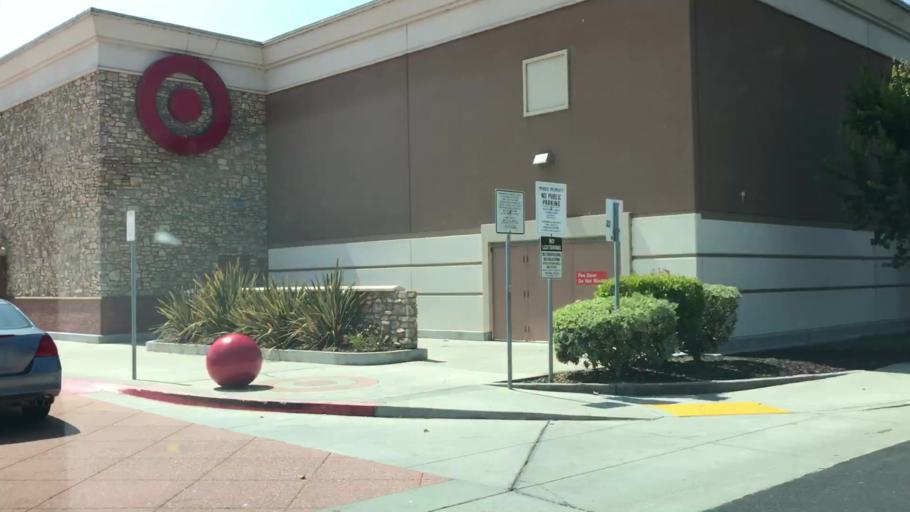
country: US
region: California
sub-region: Alameda County
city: San Lorenzo
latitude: 37.6672
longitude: -122.1207
